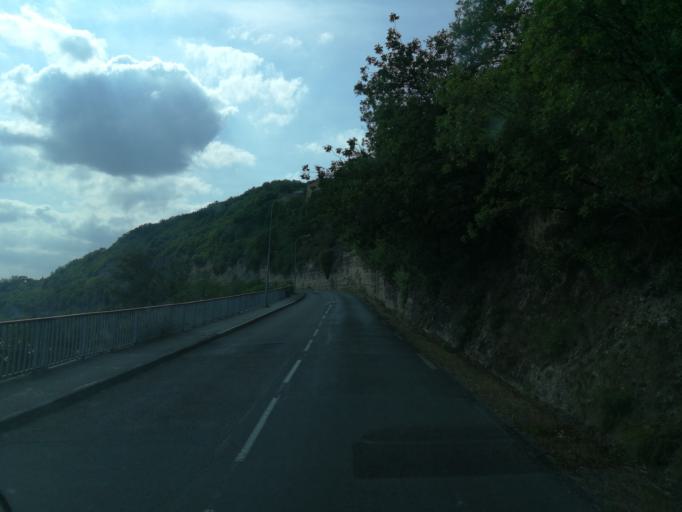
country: FR
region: Aquitaine
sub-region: Departement du Lot-et-Garonne
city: Fumel
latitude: 44.4983
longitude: 0.9822
